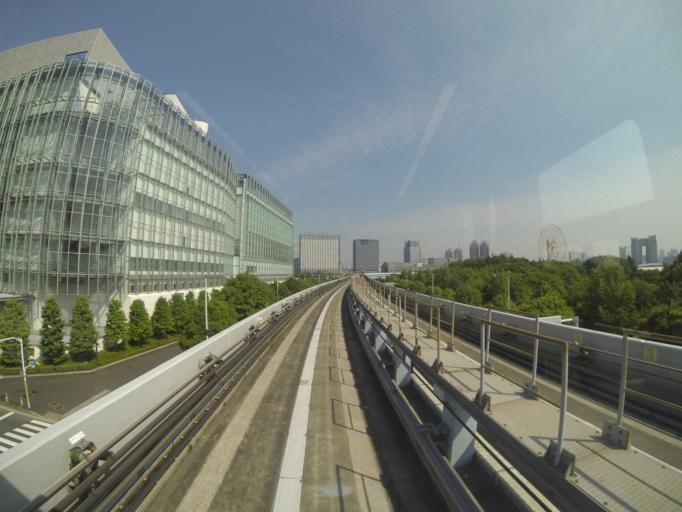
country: JP
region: Tokyo
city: Tokyo
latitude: 35.6189
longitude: 139.7811
